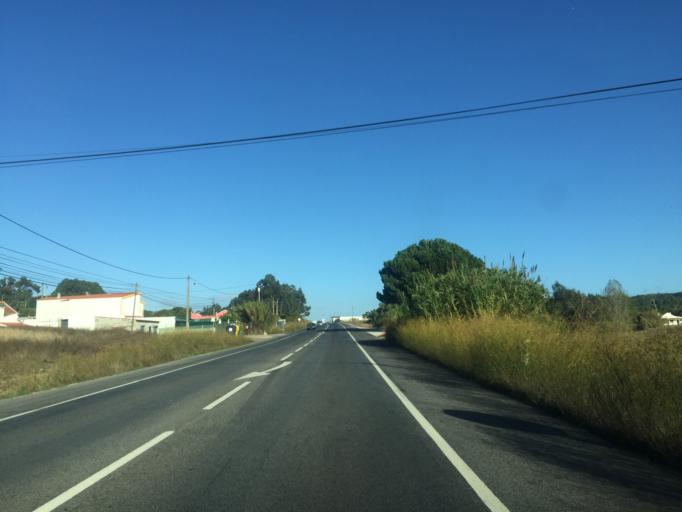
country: PT
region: Lisbon
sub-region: Azambuja
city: Aveiras de Cima
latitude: 39.1597
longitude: -8.9153
